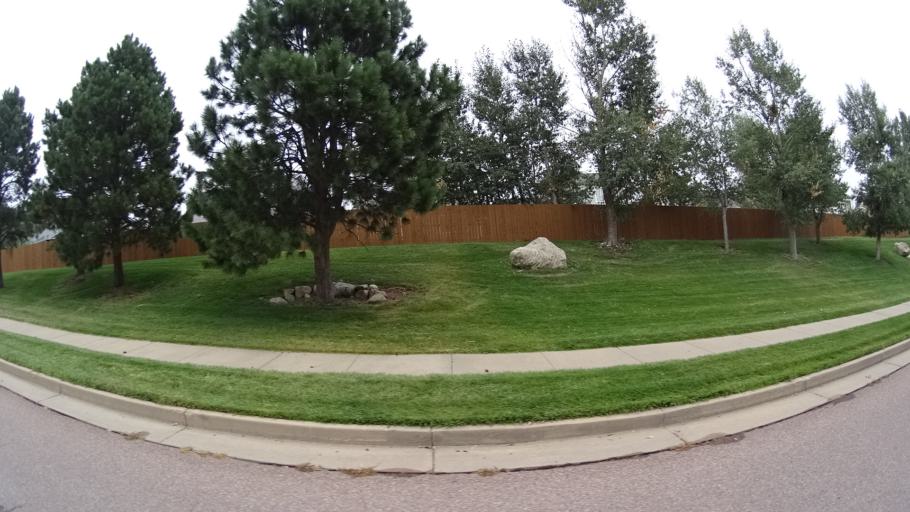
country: US
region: Colorado
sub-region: El Paso County
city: Cimarron Hills
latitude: 38.9111
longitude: -104.7112
